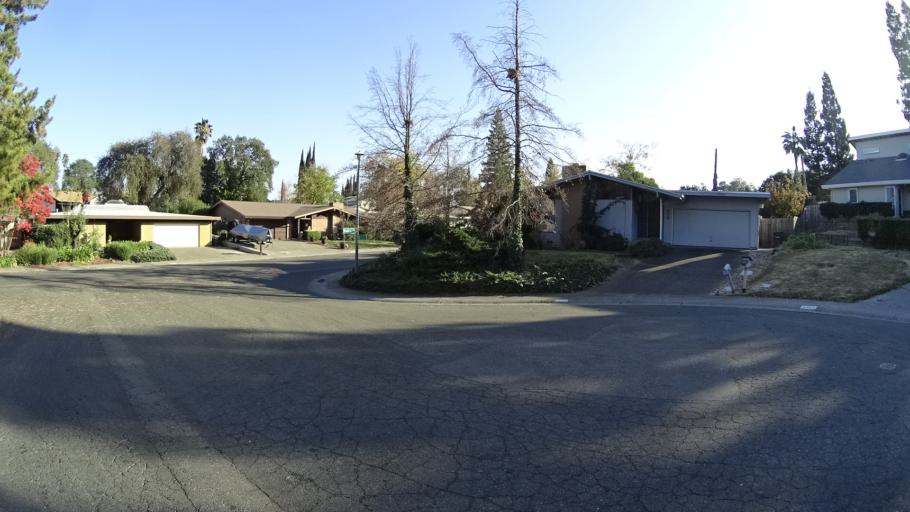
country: US
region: California
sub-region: Sacramento County
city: Fair Oaks
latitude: 38.6737
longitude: -121.2817
